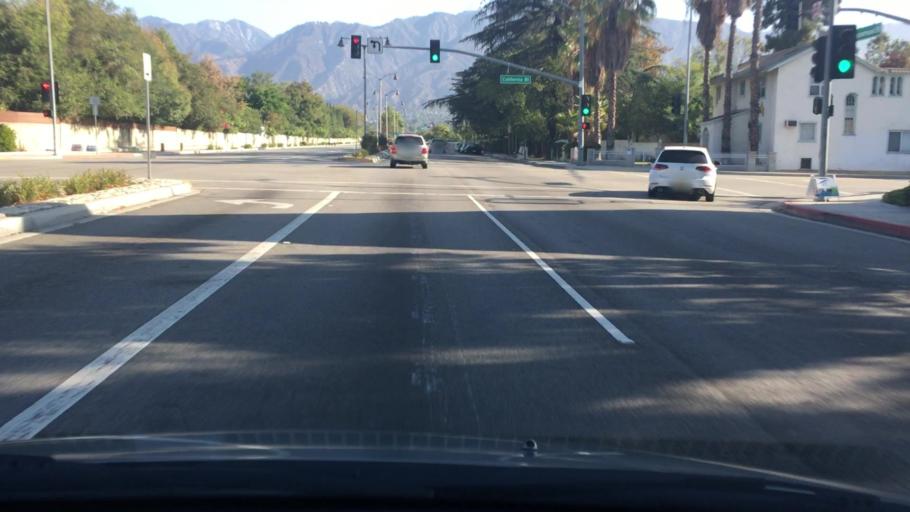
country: US
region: California
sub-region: Los Angeles County
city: East Pasadena
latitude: 34.1344
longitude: -118.0732
